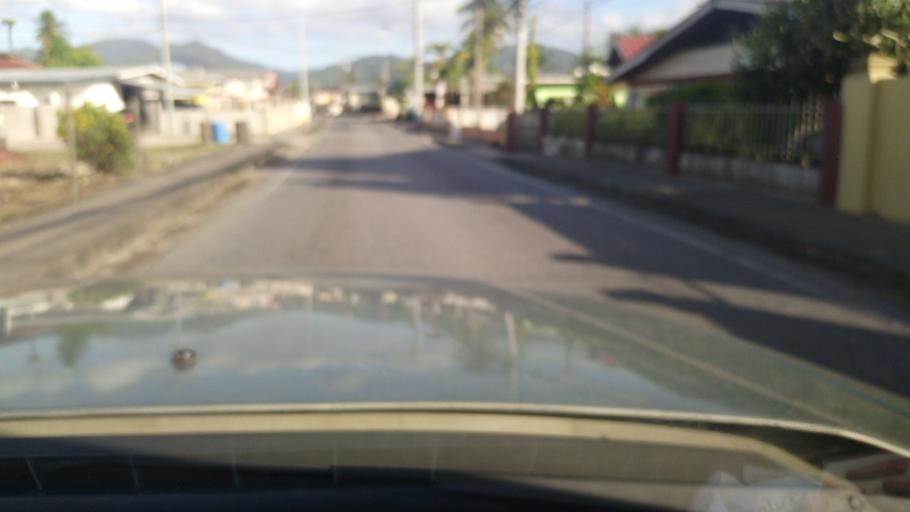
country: TT
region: Borough of Arima
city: Arima
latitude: 10.6264
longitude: -61.2741
